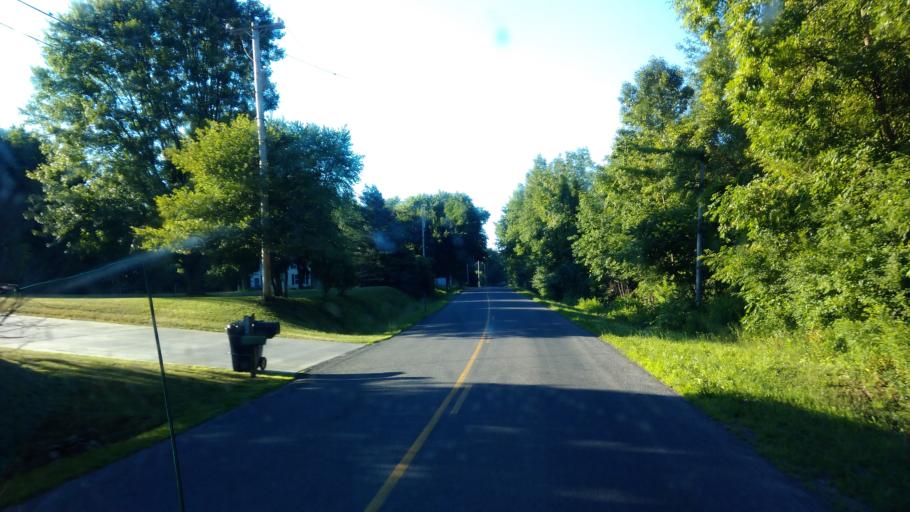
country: US
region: New York
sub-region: Wayne County
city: Lyons
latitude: 43.0860
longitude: -77.0208
